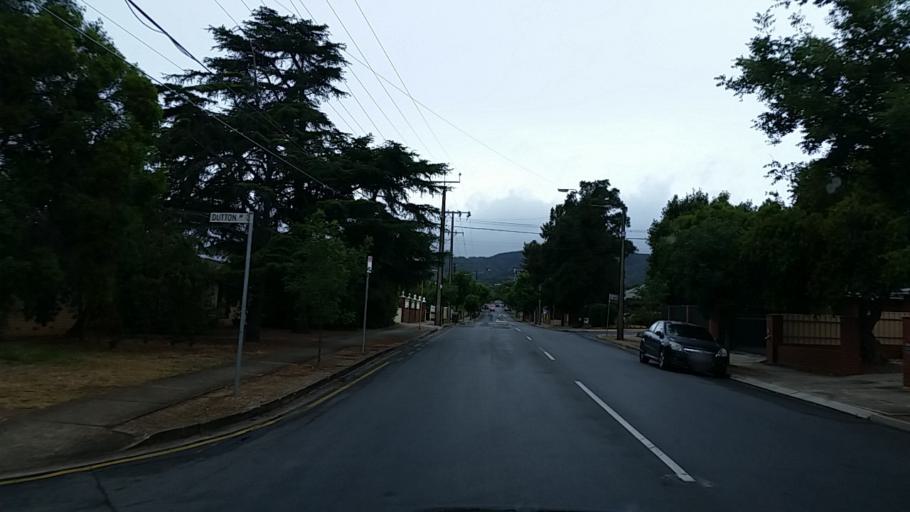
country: AU
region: South Australia
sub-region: Campbelltown
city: Hectorville
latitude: -34.8969
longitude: 138.6698
